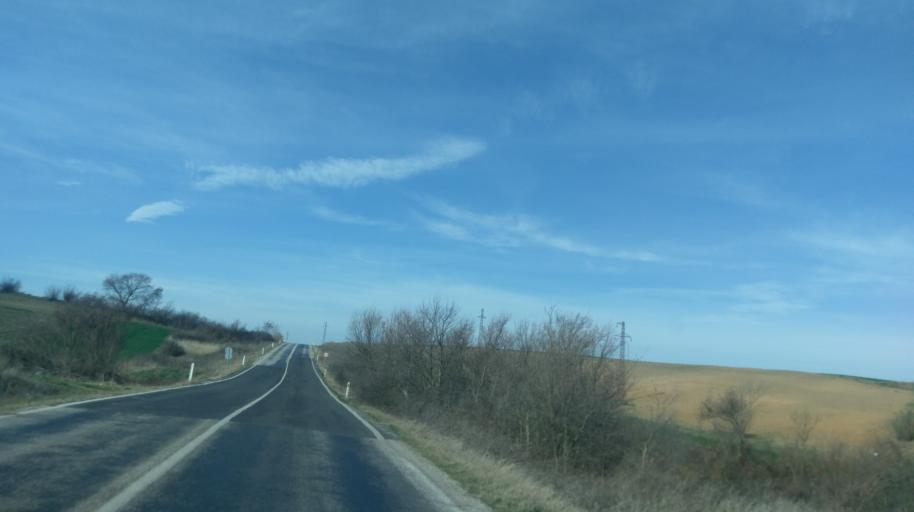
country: TR
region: Edirne
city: Uzun Keupru
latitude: 41.2759
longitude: 26.7459
